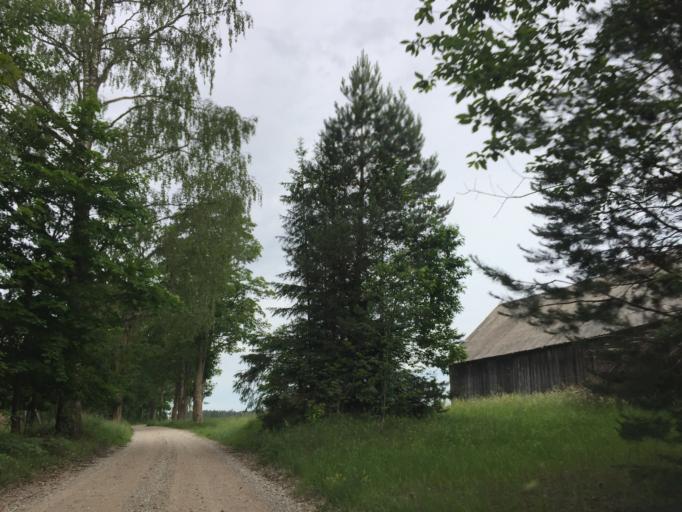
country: LV
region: Tukuma Rajons
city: Tukums
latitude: 57.0403
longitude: 23.1639
